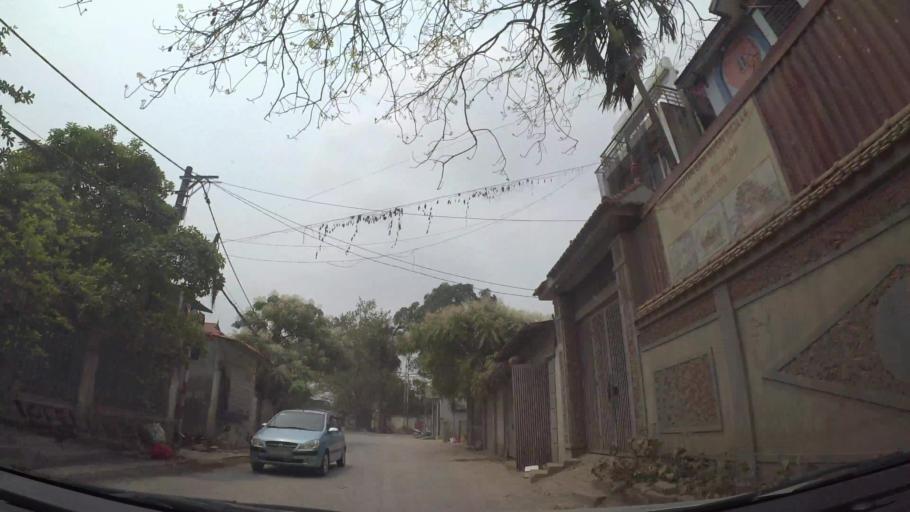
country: VN
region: Ha Noi
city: Cau Dien
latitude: 21.0305
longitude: 105.7398
